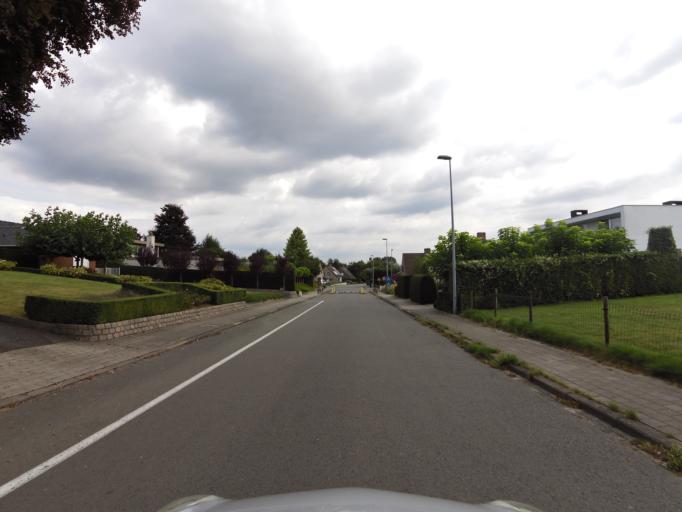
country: BE
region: Flanders
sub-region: Provincie West-Vlaanderen
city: Tielt
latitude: 50.9950
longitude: 3.3414
